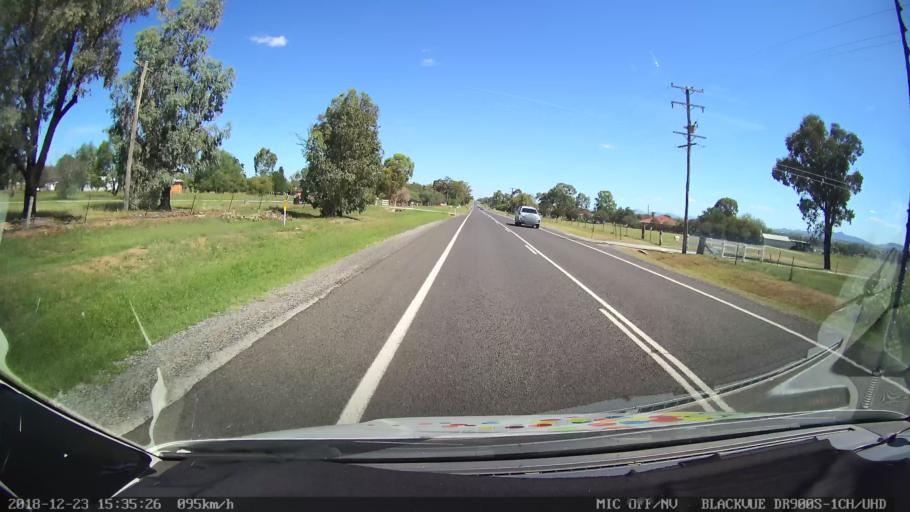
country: AU
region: New South Wales
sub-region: Tamworth Municipality
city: Tamworth
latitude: -31.0273
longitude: 150.8825
